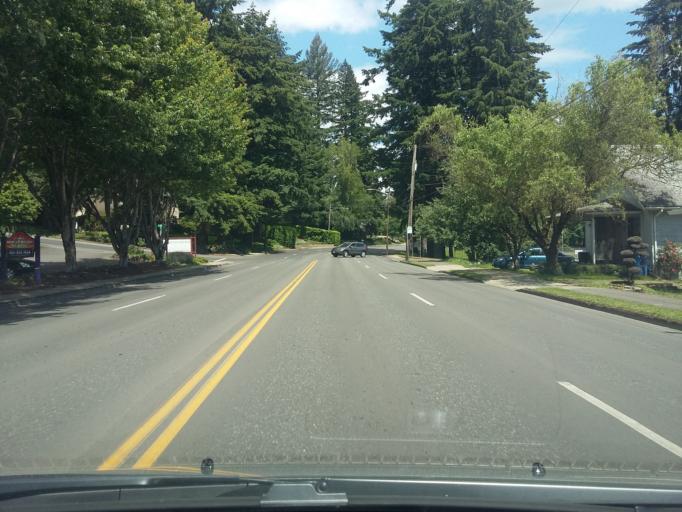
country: US
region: Washington
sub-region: Clark County
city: Camas
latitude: 45.5879
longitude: -122.3984
